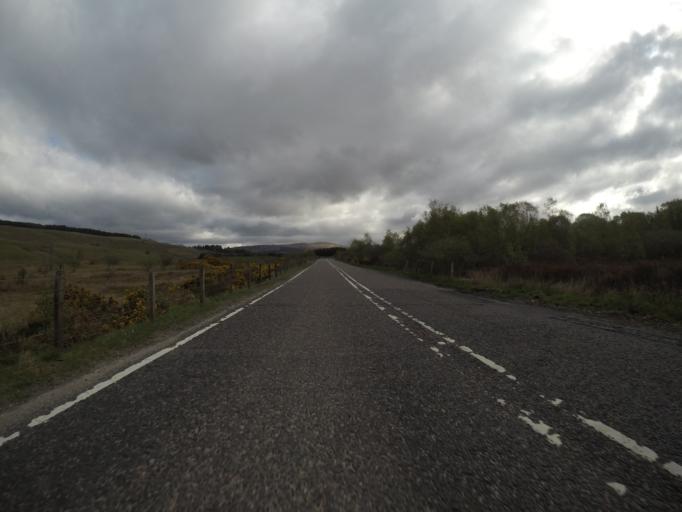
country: GB
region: Scotland
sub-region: Highland
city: Spean Bridge
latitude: 56.8764
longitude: -4.9780
